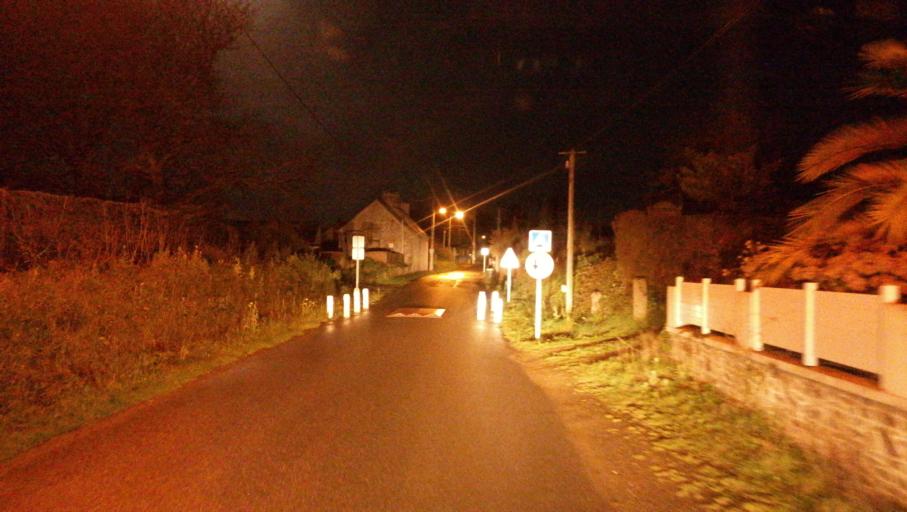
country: FR
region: Brittany
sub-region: Departement des Cotes-d'Armor
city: Plouha
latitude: 48.6720
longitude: -2.9480
